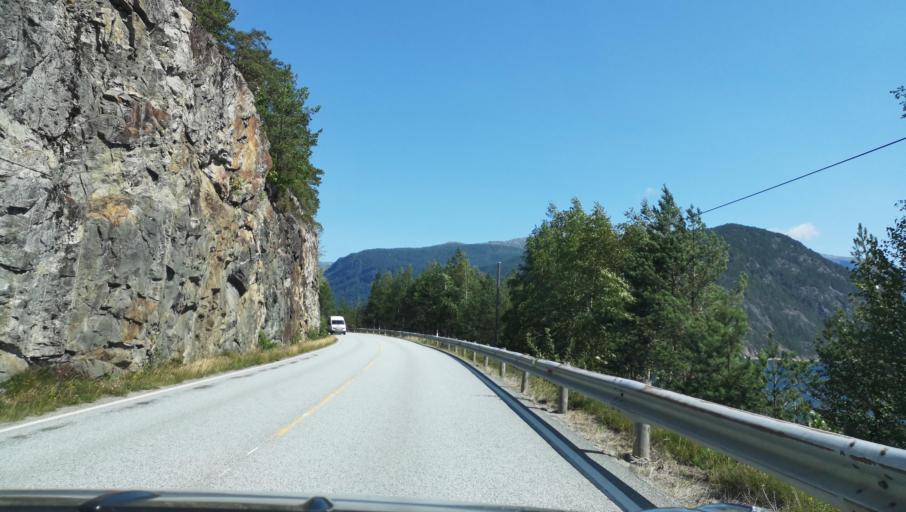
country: NO
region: Hordaland
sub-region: Ulvik
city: Ulvik
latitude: 60.4900
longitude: 6.8909
